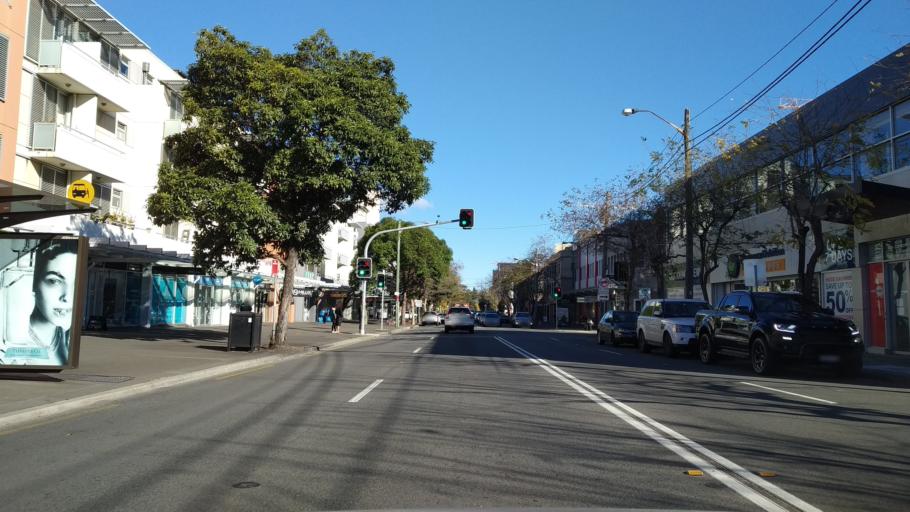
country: AU
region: New South Wales
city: Alexandria
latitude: -33.9143
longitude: 151.2010
